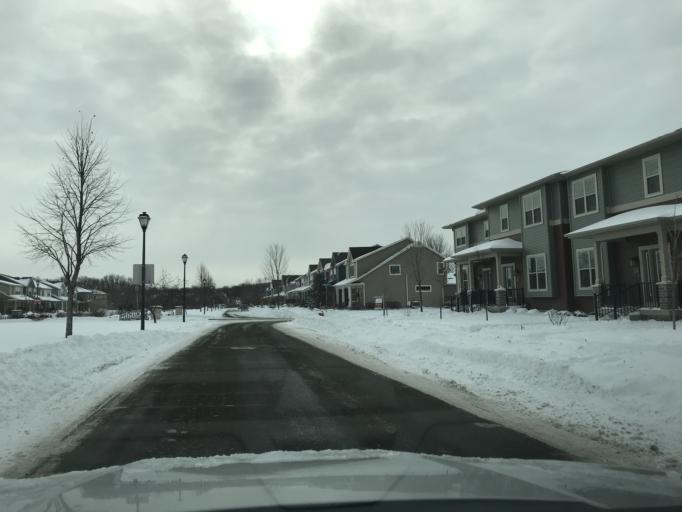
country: US
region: Wisconsin
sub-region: Dane County
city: Sun Prairie
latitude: 43.1602
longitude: -89.2624
